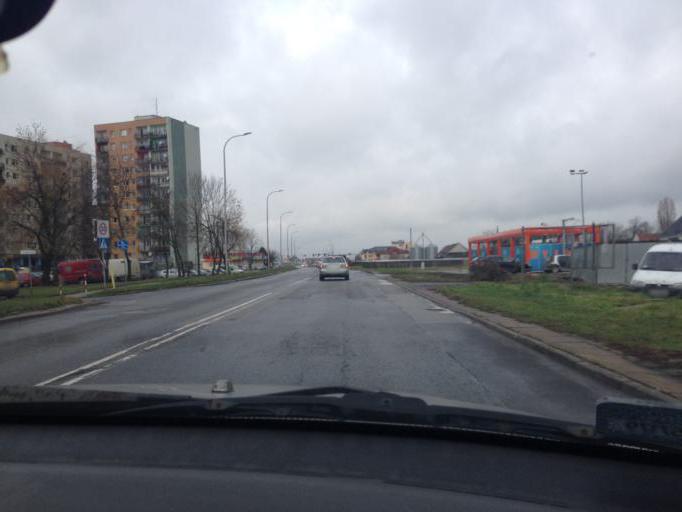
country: PL
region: Opole Voivodeship
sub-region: Powiat opolski
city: Opole
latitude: 50.6840
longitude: 17.9537
